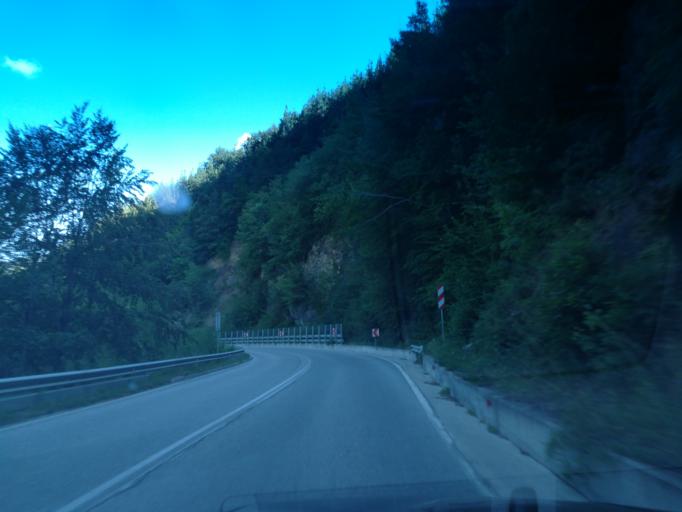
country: BG
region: Smolyan
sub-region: Obshtina Chepelare
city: Chepelare
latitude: 41.8163
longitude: 24.7008
